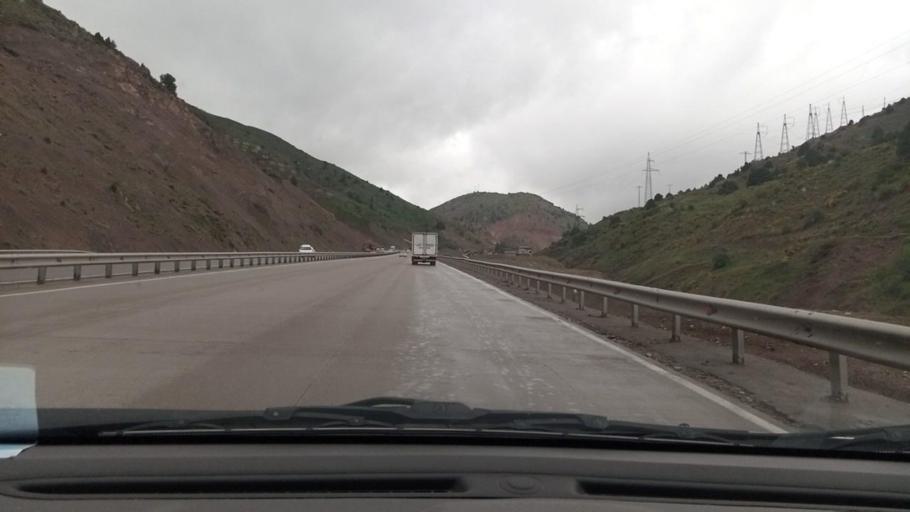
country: UZ
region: Toshkent
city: Angren
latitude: 41.0560
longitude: 70.5643
